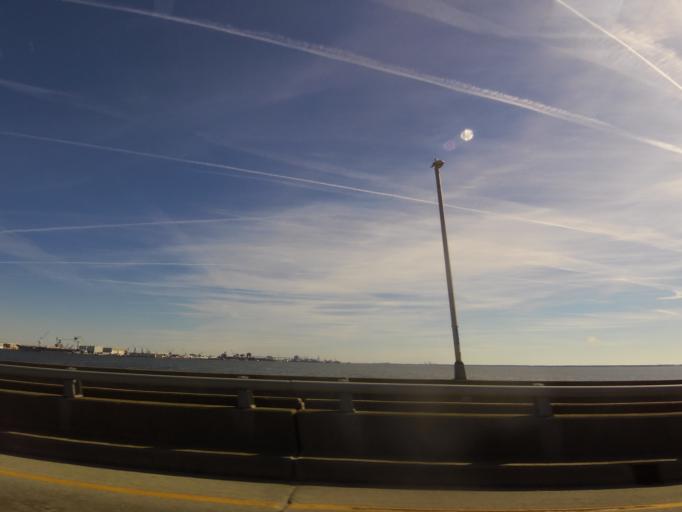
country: US
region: Virginia
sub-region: City of Newport News
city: Newport News
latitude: 36.9970
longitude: -76.4761
